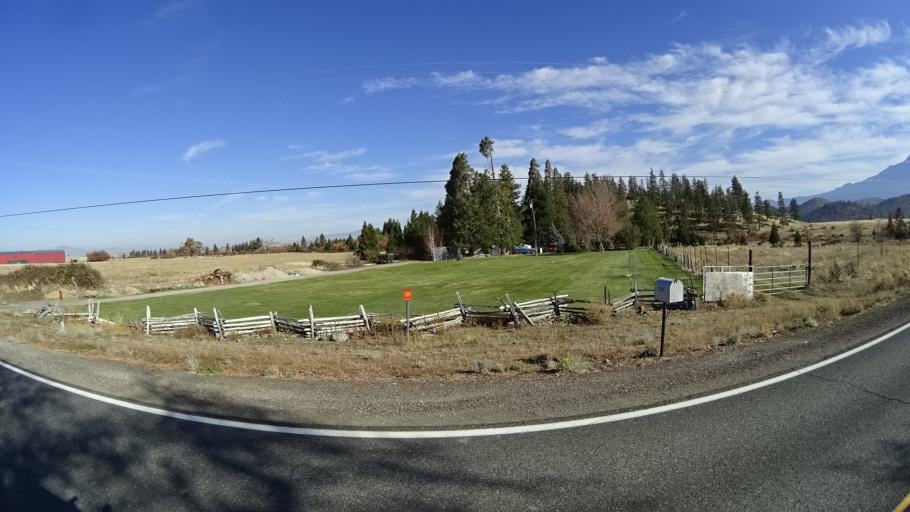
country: US
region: California
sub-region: Siskiyou County
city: Weed
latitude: 41.4482
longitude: -122.4503
